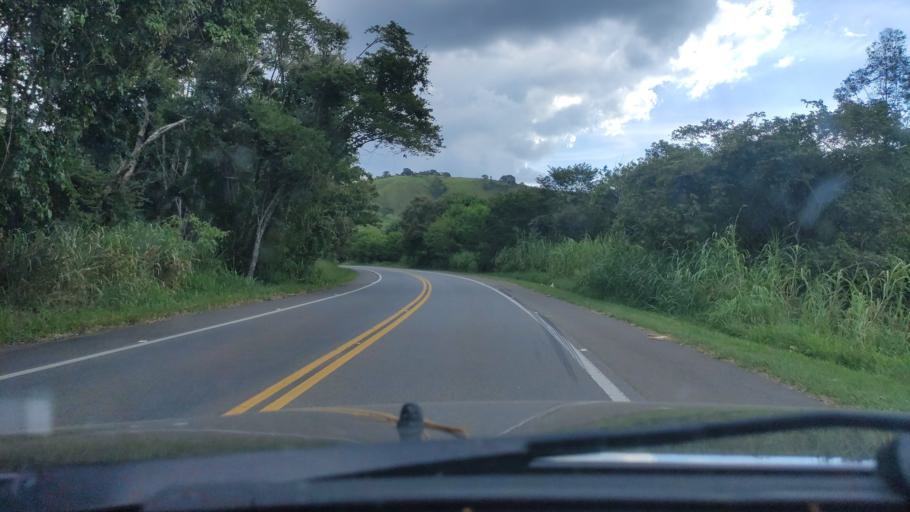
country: BR
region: Sao Paulo
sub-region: Aguas De Lindoia
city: Aguas de Lindoia
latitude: -22.4690
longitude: -46.7017
